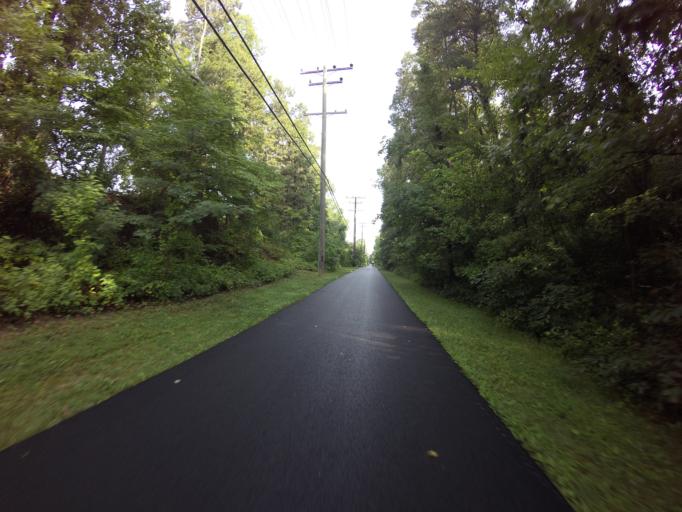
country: US
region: Maryland
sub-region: Anne Arundel County
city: Pasadena
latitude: 39.1113
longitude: -76.5787
